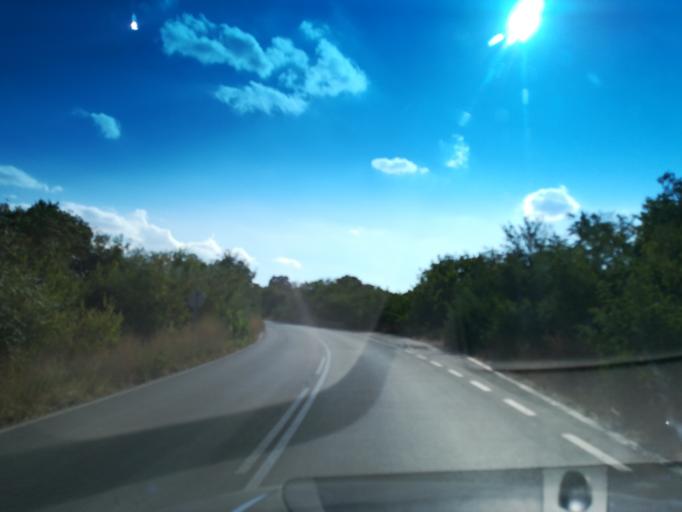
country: BG
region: Khaskovo
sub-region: Obshtina Mineralni Bani
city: Mineralni Bani
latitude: 42.0132
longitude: 25.3985
